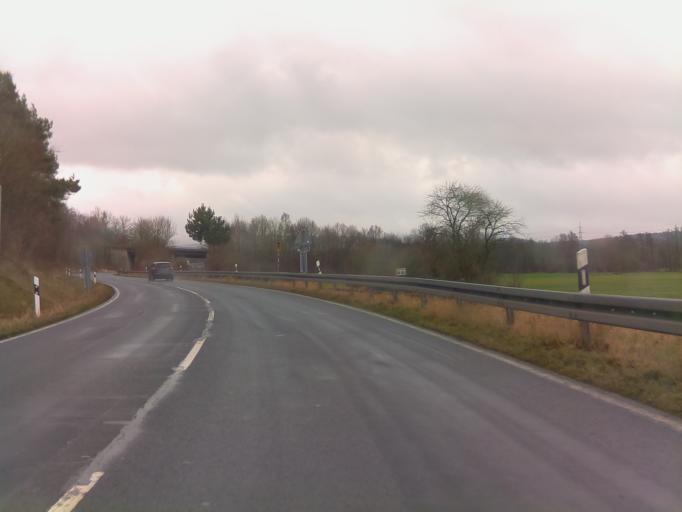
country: DE
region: Hesse
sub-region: Regierungsbezirk Kassel
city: Eichenzell
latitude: 50.5051
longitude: 9.6816
